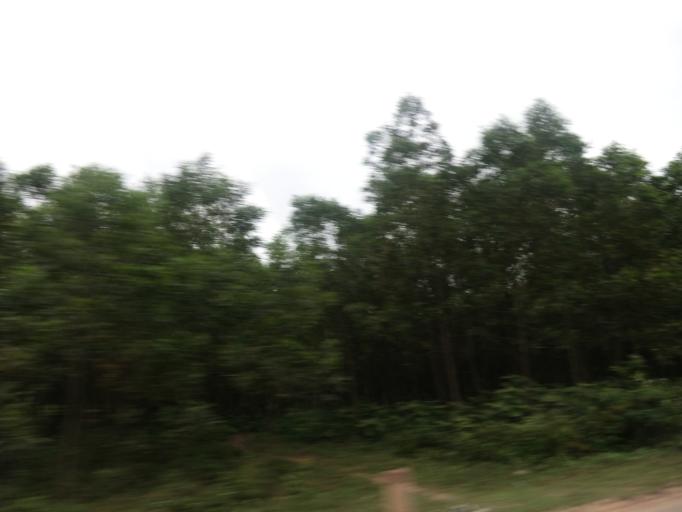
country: VN
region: Quang Tri
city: Cam Lo
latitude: 16.8494
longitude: 106.9985
